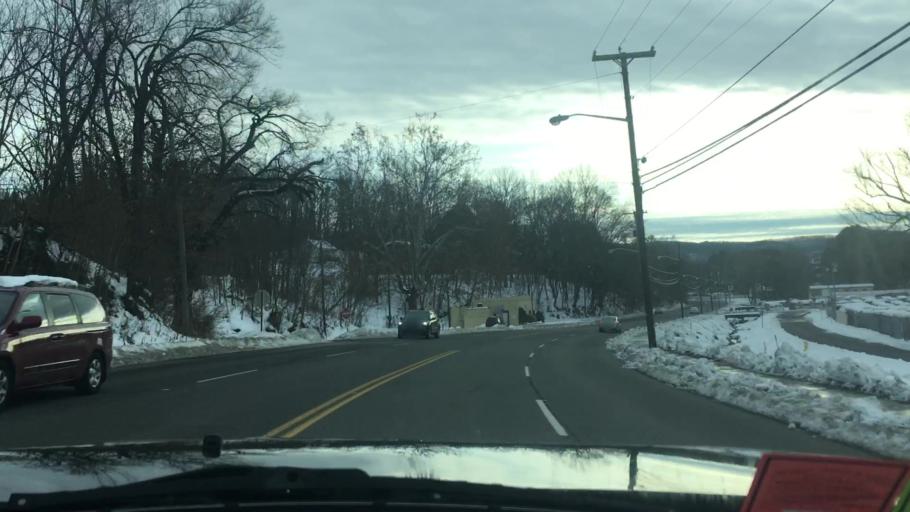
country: US
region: Virginia
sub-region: Pulaski County
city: Pulaski
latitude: 37.0575
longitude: -80.7720
